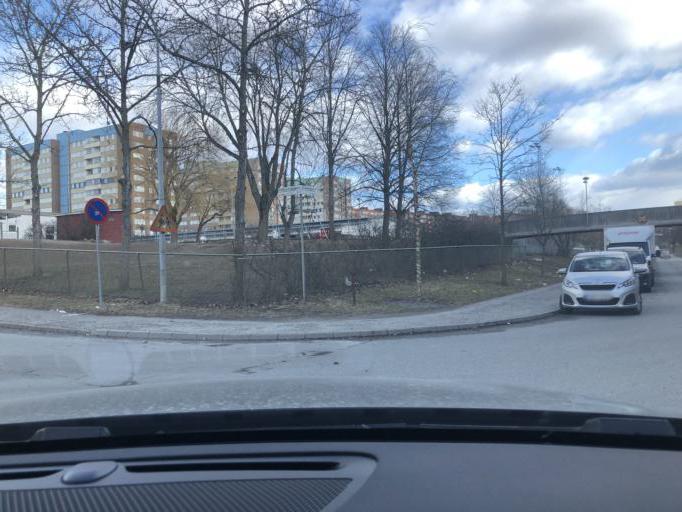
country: SE
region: Stockholm
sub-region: Stockholms Kommun
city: Kista
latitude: 59.4125
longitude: 17.9171
